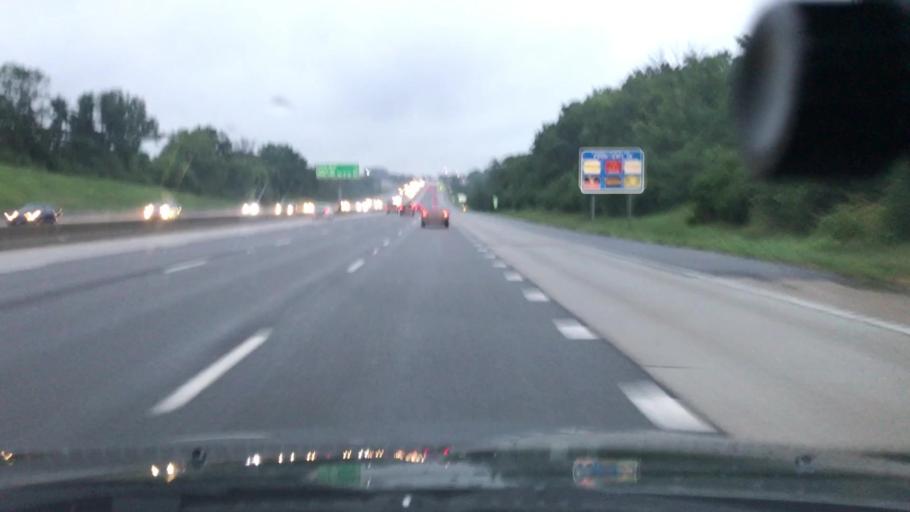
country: US
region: Missouri
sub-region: Saint Louis County
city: Maryland Heights
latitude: 38.6850
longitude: -90.4501
